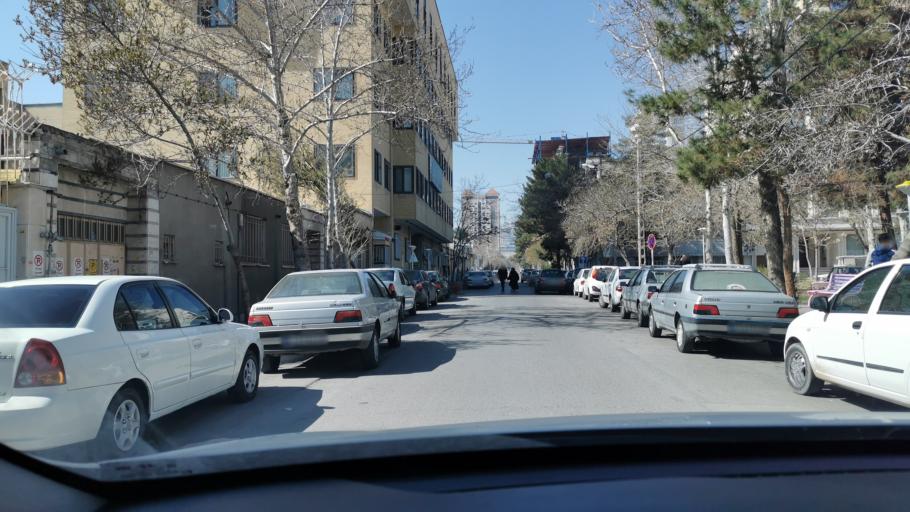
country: IR
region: Razavi Khorasan
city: Mashhad
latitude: 36.2892
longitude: 59.5770
